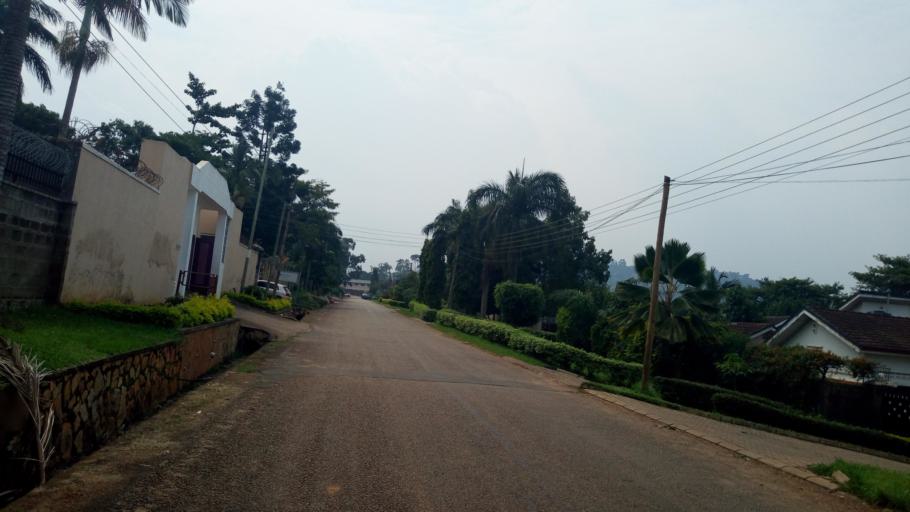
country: UG
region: Central Region
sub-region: Wakiso District
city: Kireka
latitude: 0.3100
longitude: 32.6286
